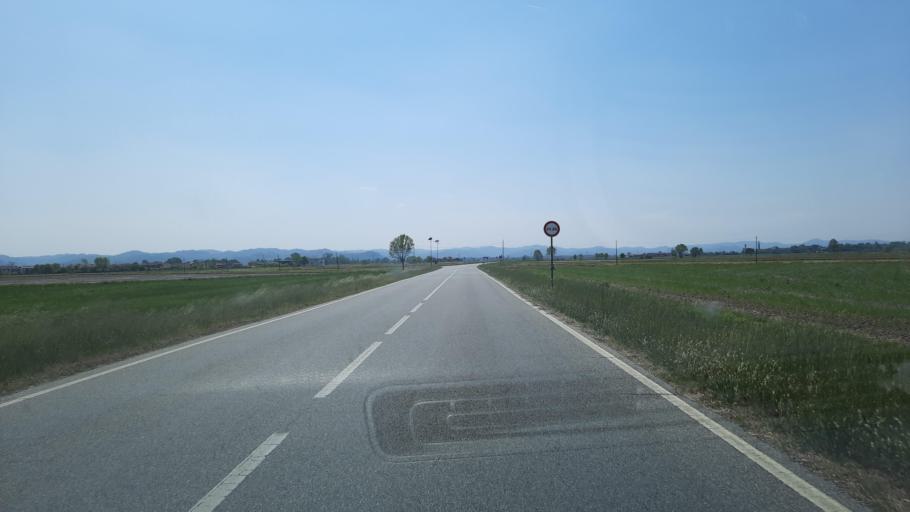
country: IT
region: Piedmont
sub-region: Provincia di Vercelli
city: Lamporo
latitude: 45.2230
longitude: 8.1447
